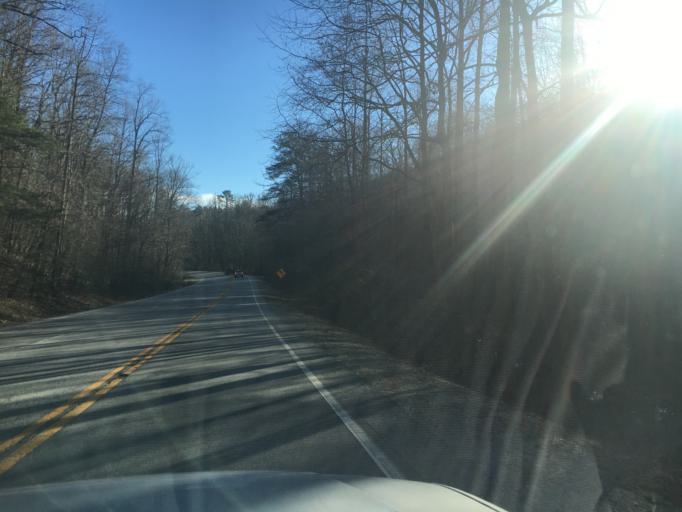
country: US
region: Georgia
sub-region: Union County
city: Blairsville
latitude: 34.7032
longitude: -83.9157
